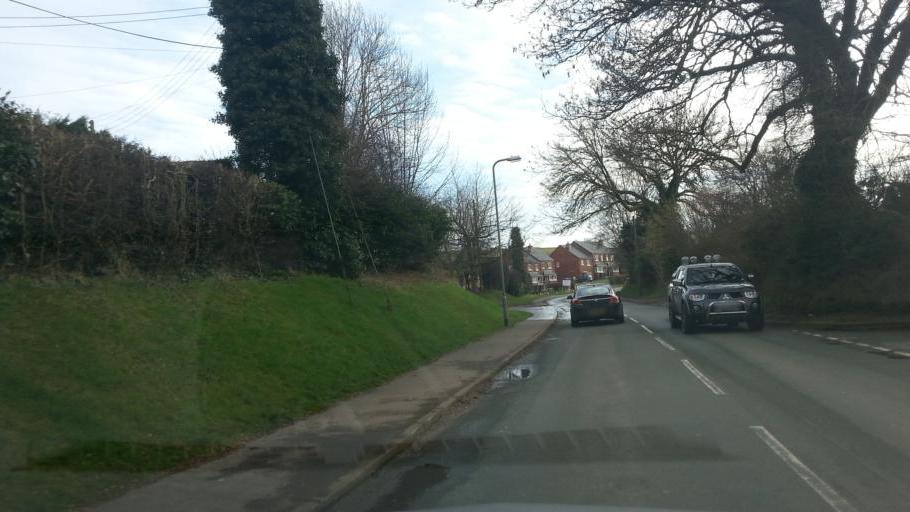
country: GB
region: England
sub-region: Staffordshire
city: Colwich
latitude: 52.8289
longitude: -1.9993
